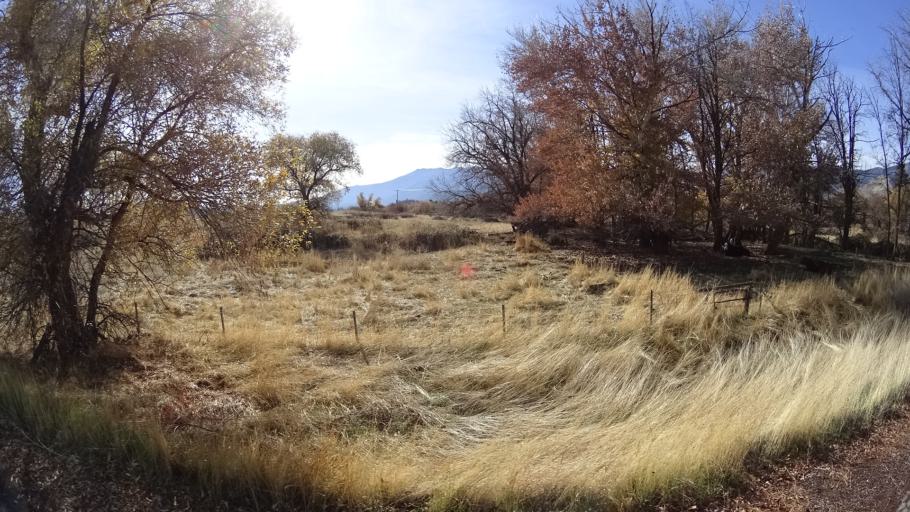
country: US
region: California
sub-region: Siskiyou County
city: Weed
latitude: 41.4711
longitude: -122.4387
